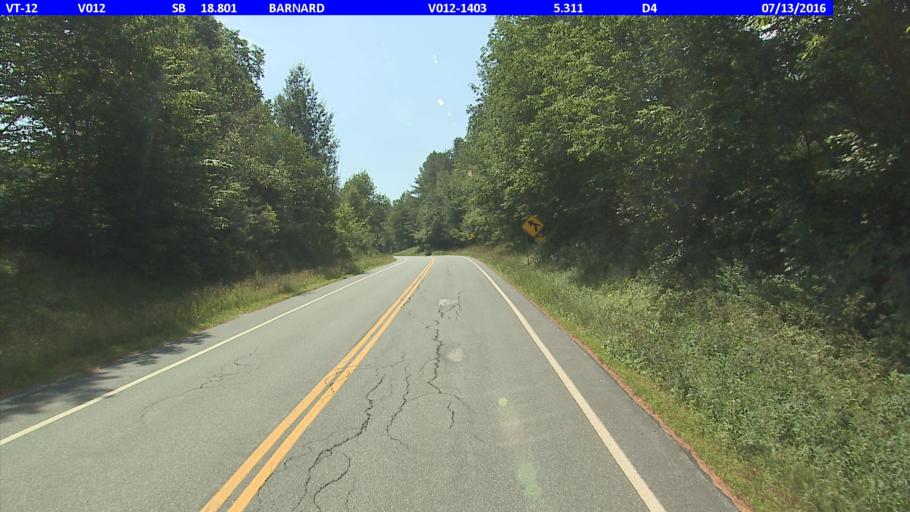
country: US
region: Vermont
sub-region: Windsor County
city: Woodstock
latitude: 43.7345
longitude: -72.6257
